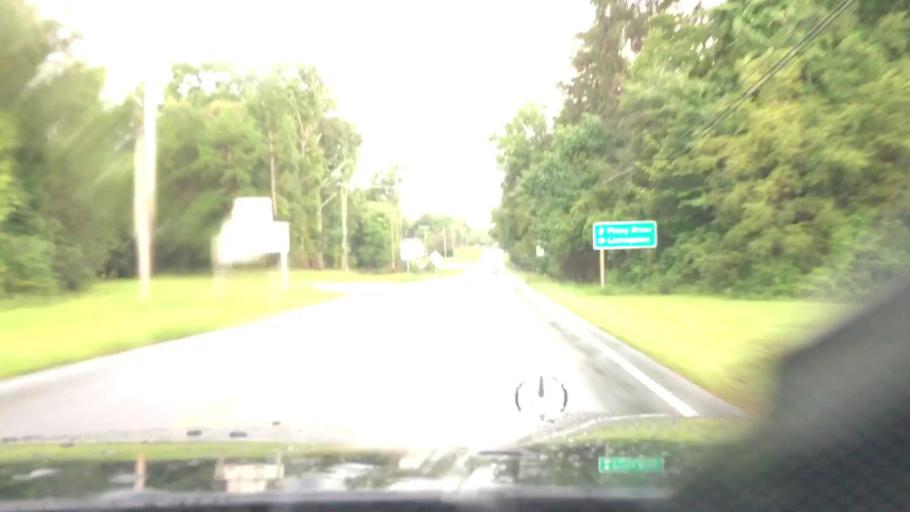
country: US
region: Virginia
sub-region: Amherst County
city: Amherst
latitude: 37.7252
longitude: -79.0130
